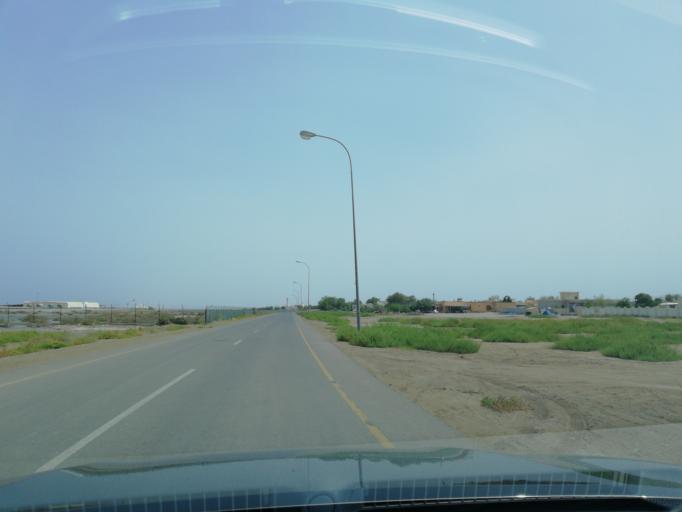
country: OM
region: Al Batinah
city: Shinas
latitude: 24.7527
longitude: 56.4672
